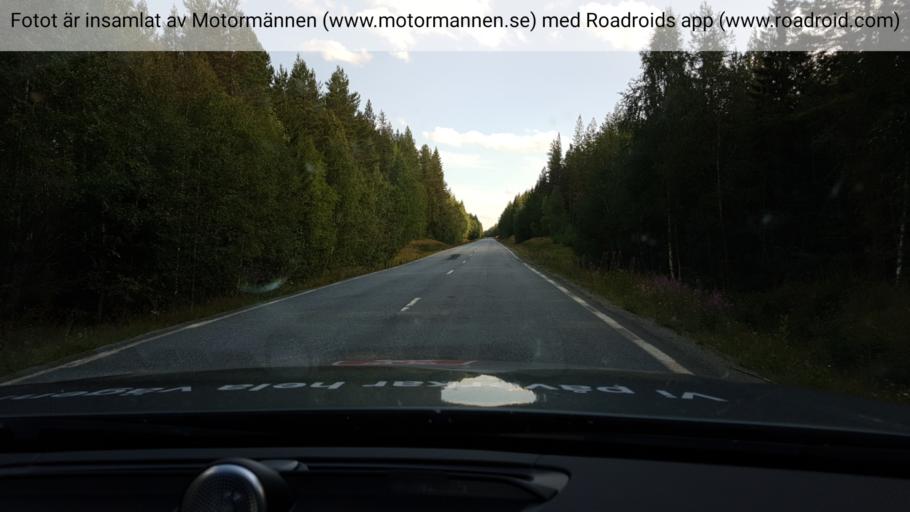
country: SE
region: Vaesterbotten
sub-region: Dorotea Kommun
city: Dorotea
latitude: 63.8823
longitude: 16.3720
